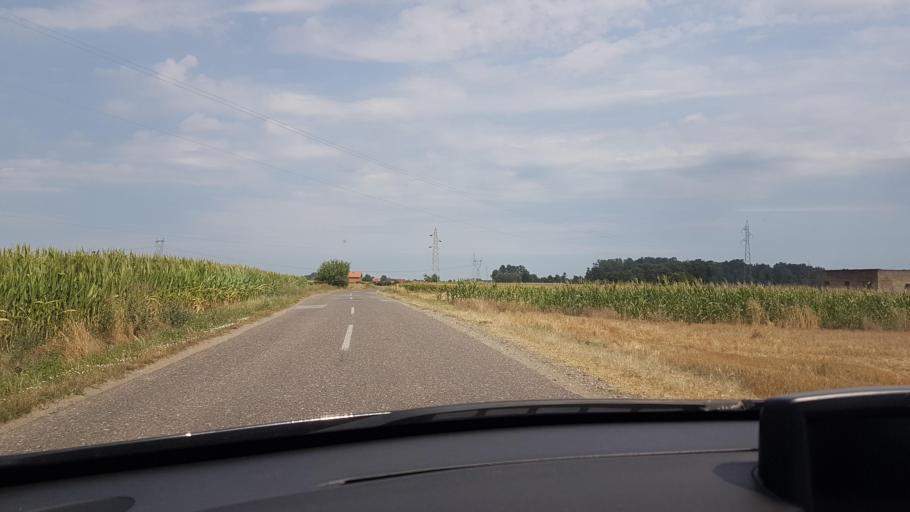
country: BA
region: Republika Srpska
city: Bijeljina
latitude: 44.7932
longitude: 19.2210
